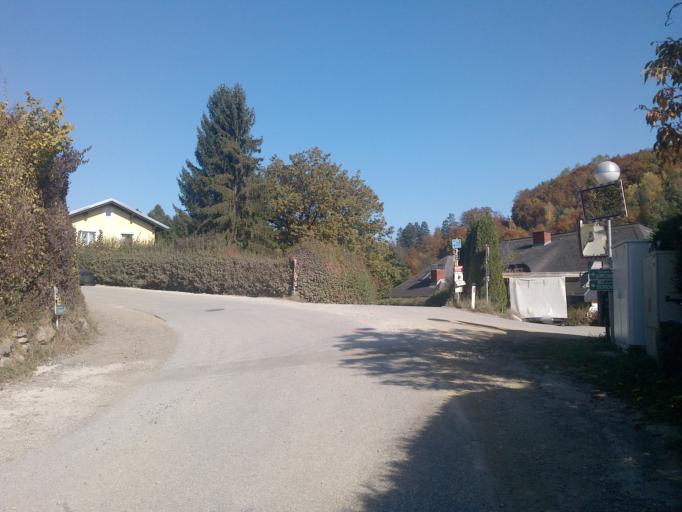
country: AT
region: Styria
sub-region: Politischer Bezirk Graz-Umgebung
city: Pirka
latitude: 47.0197
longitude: 15.3576
